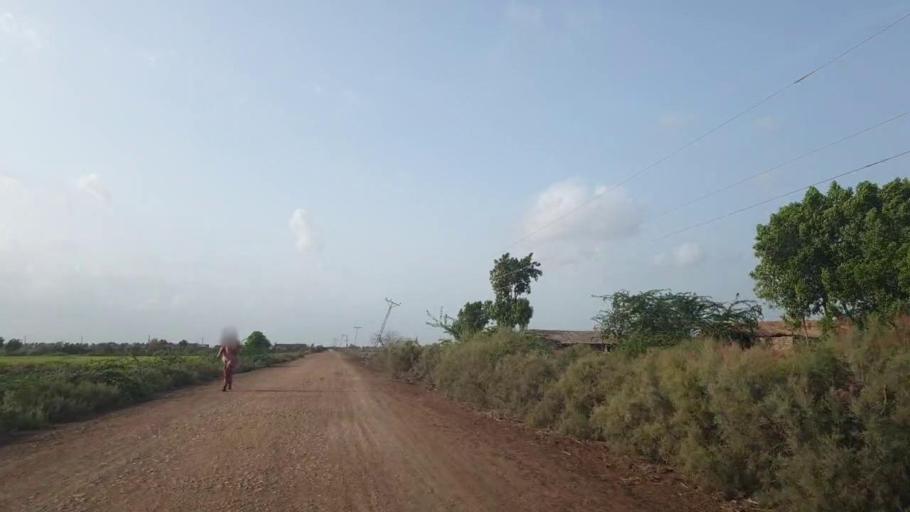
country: PK
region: Sindh
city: Tando Bago
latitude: 24.6489
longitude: 69.1119
